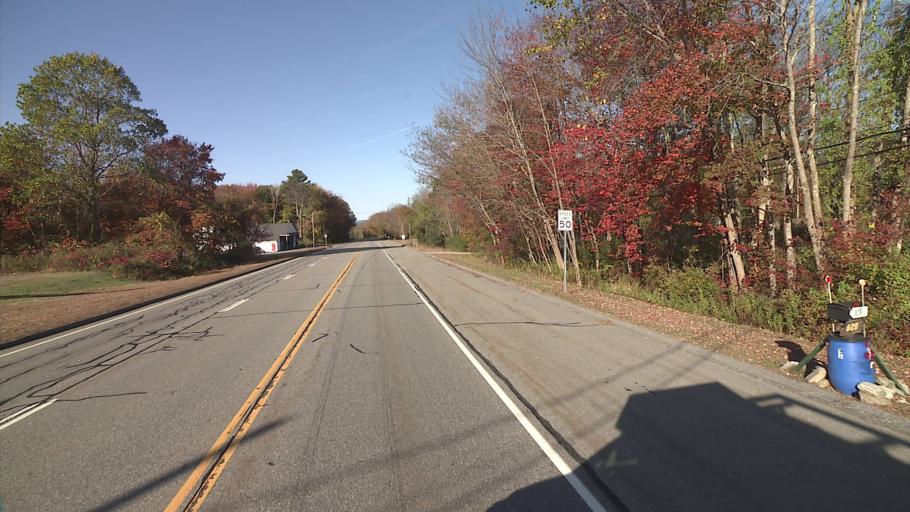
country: US
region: Connecticut
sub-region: Windham County
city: Danielson
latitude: 41.7909
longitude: -71.8217
